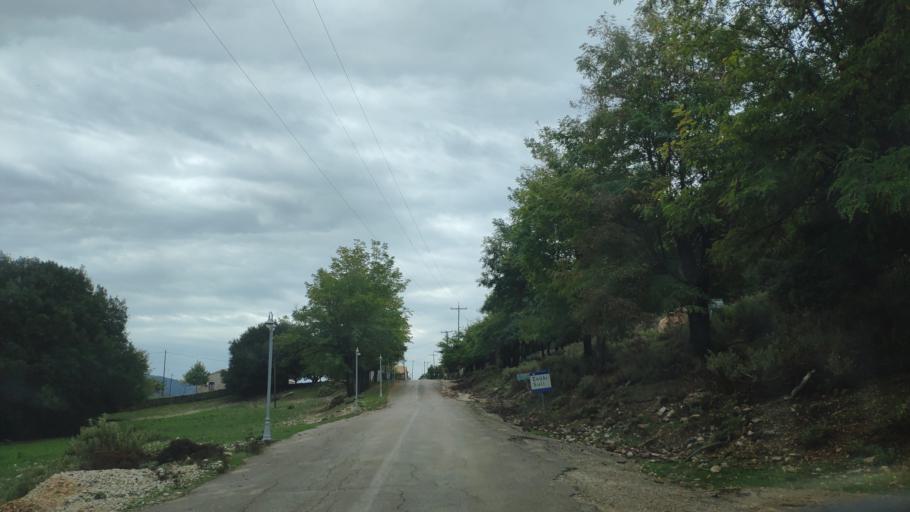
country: GR
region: Epirus
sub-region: Nomos Prevezis
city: Kanalaki
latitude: 39.3610
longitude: 20.6407
